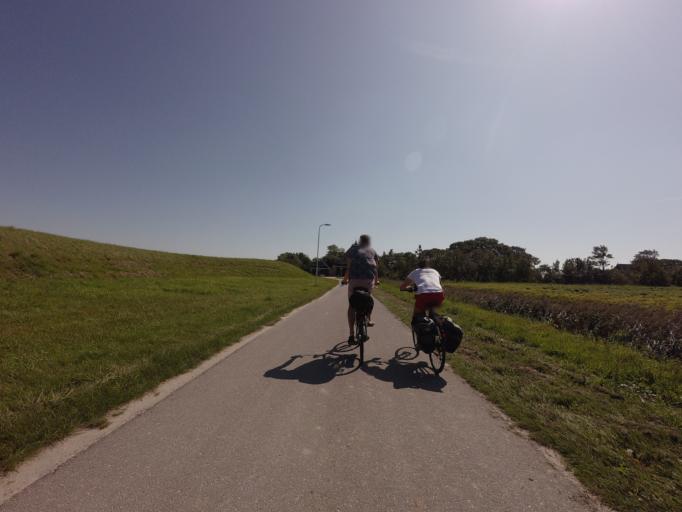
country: NL
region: Friesland
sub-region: Gemeente Dongeradeel
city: Anjum
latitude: 53.3951
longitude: 6.1092
